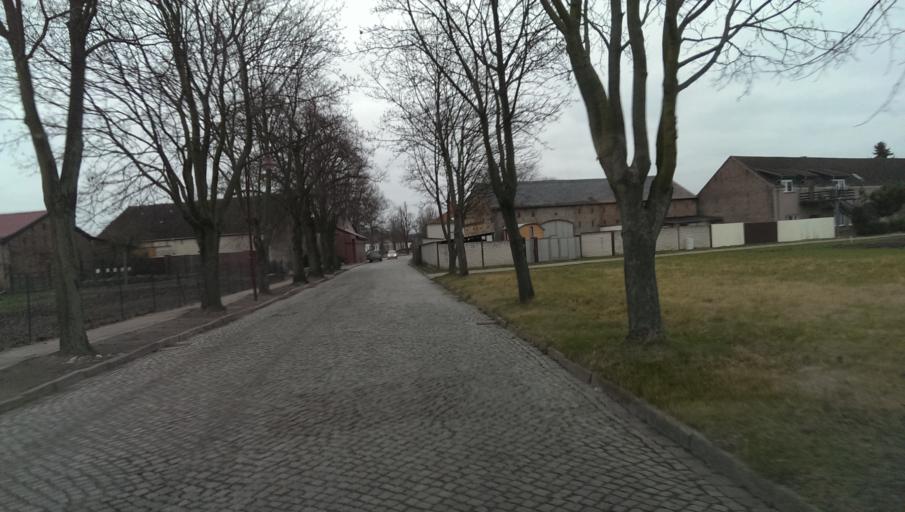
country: DE
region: Brandenburg
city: Mittenwalde
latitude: 52.2249
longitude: 13.5084
